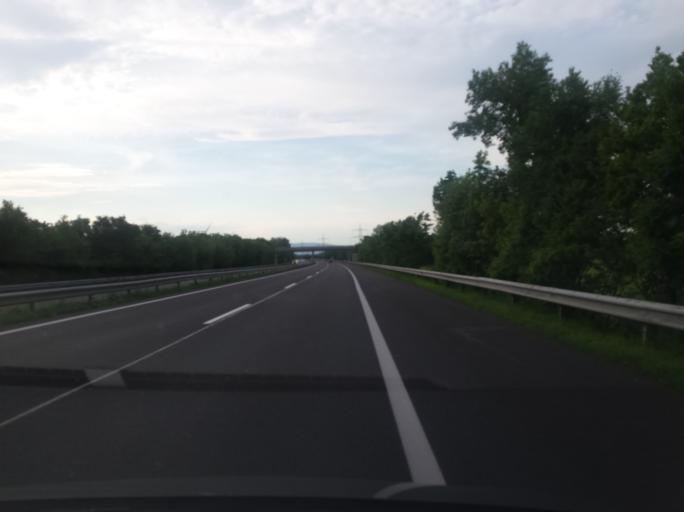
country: AT
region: Lower Austria
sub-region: Politischer Bezirk Baden
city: Pottendorf
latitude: 47.9192
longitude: 16.4032
